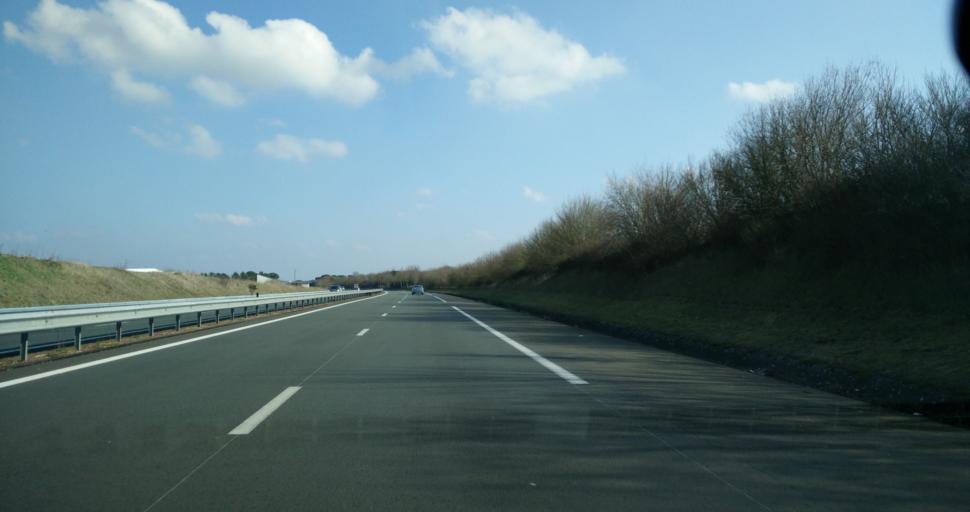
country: FR
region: Poitou-Charentes
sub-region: Departement de la Charente-Maritime
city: Saint-Jean-de-Liversay
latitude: 46.2242
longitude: -0.8580
